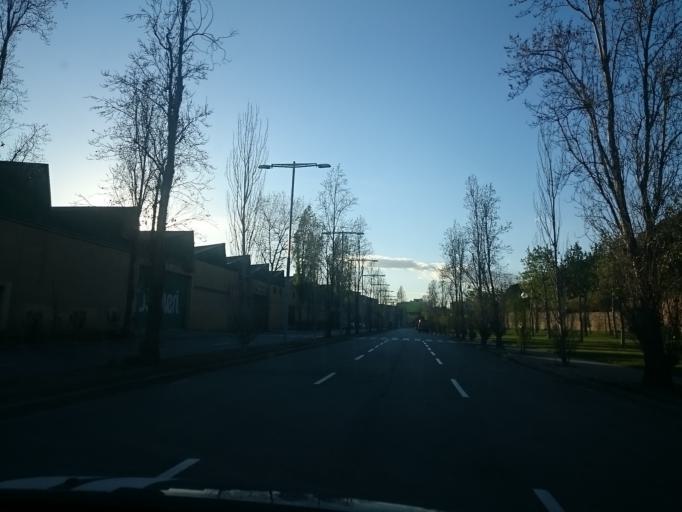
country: ES
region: Catalonia
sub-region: Provincia de Barcelona
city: Sants-Montjuic
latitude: 41.3536
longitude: 2.1494
